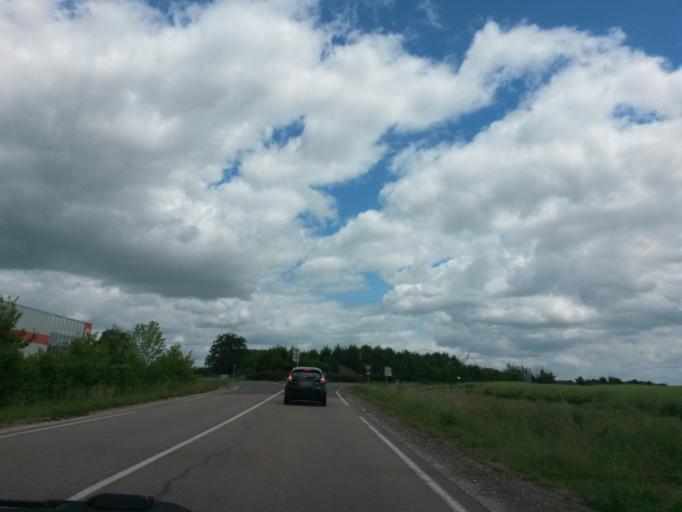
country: FR
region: Bourgogne
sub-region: Departement de la Nievre
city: Cosne-Cours-sur-Loire
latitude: 47.3843
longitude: 2.9288
